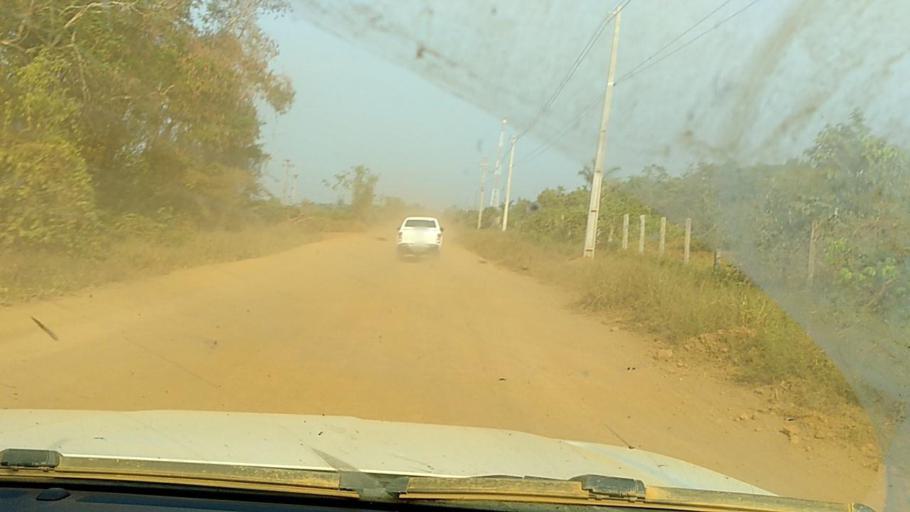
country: BR
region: Rondonia
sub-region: Porto Velho
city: Porto Velho
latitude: -8.7603
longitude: -63.9672
